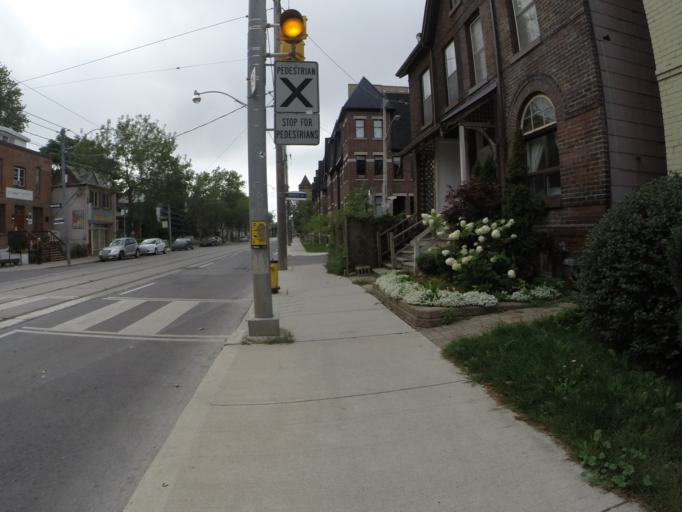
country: CA
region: Ontario
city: Toronto
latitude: 43.6618
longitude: -79.3512
